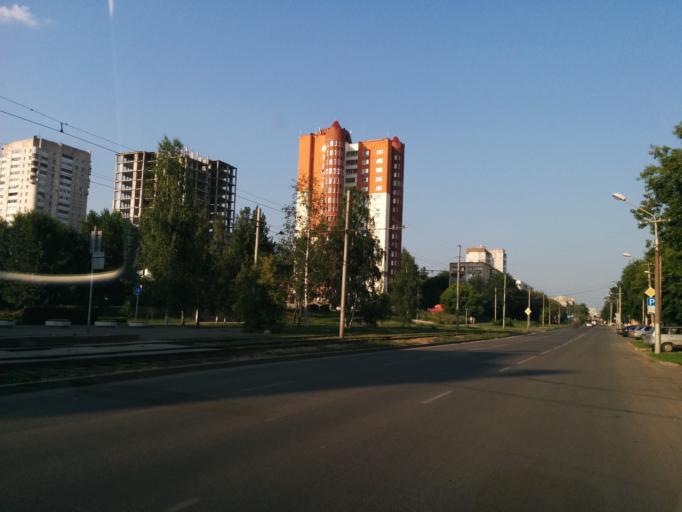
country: RU
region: Perm
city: Perm
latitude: 58.0058
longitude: 56.1981
